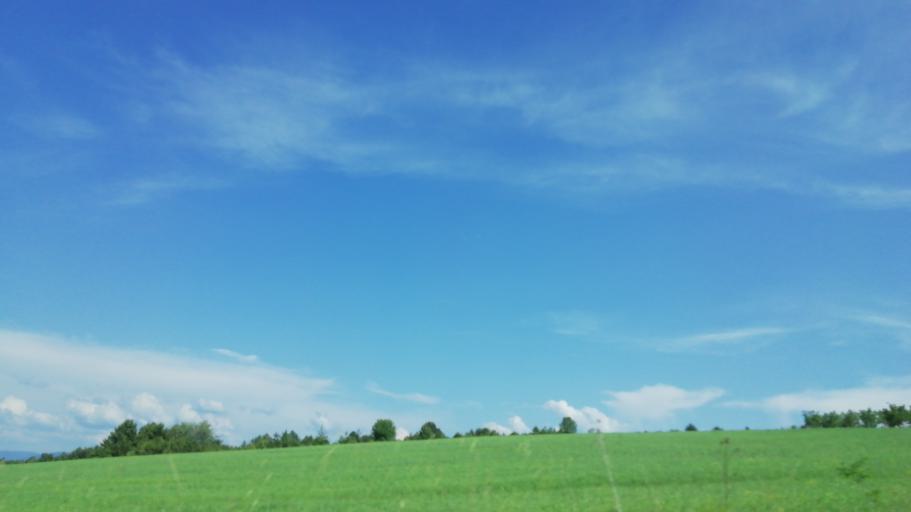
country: TR
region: Karabuk
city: Karabuk
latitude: 41.0916
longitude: 32.5886
